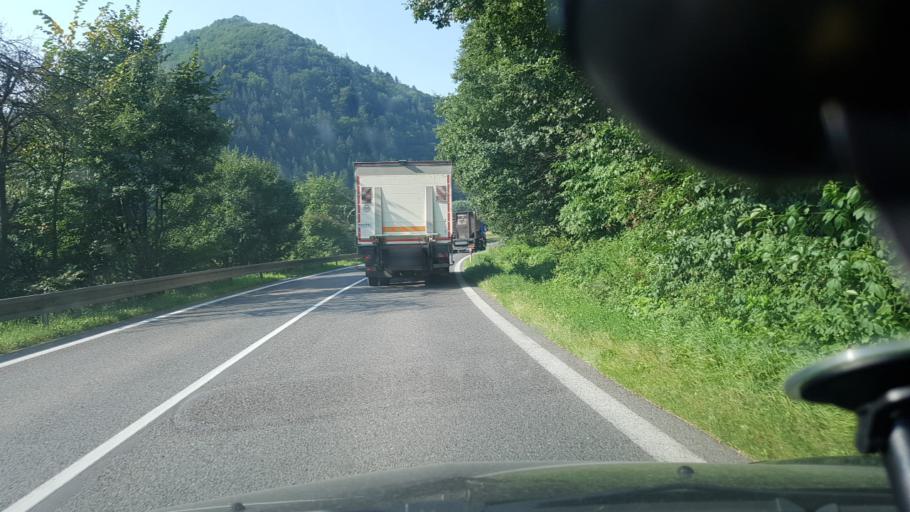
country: SK
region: Zilinsky
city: Tvrdosin
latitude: 49.2688
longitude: 19.4587
